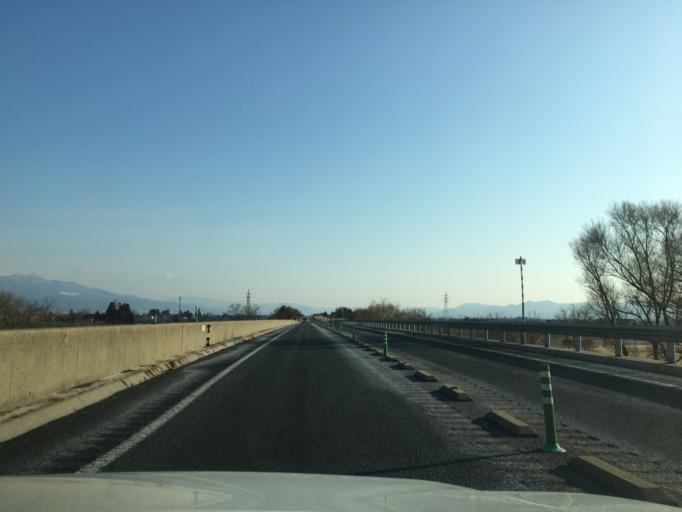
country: JP
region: Yamagata
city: Sagae
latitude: 38.3455
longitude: 140.2971
